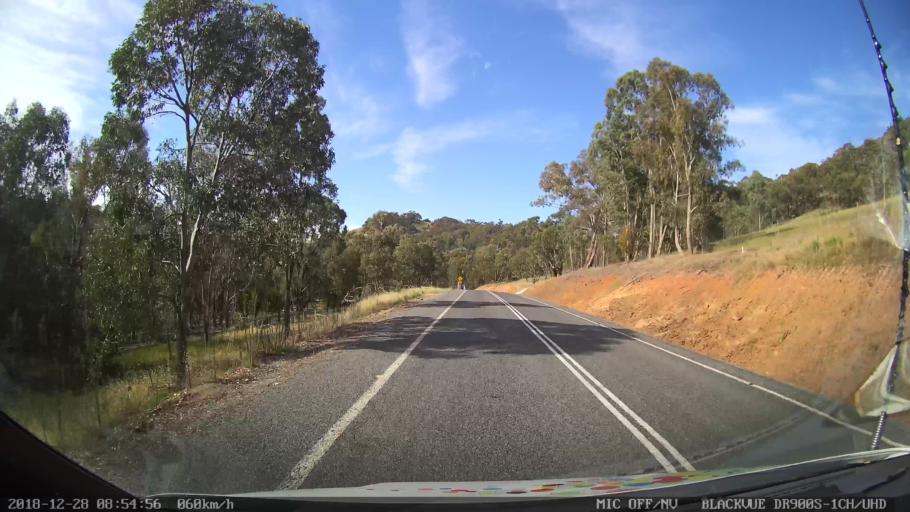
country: AU
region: New South Wales
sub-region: Upper Lachlan Shire
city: Crookwell
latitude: -34.0962
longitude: 149.3322
